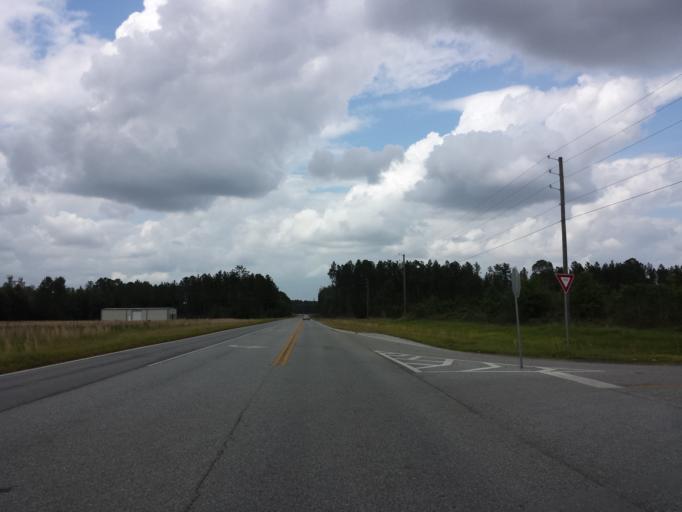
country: US
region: Georgia
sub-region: Cook County
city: Adel
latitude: 31.0929
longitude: -83.4080
